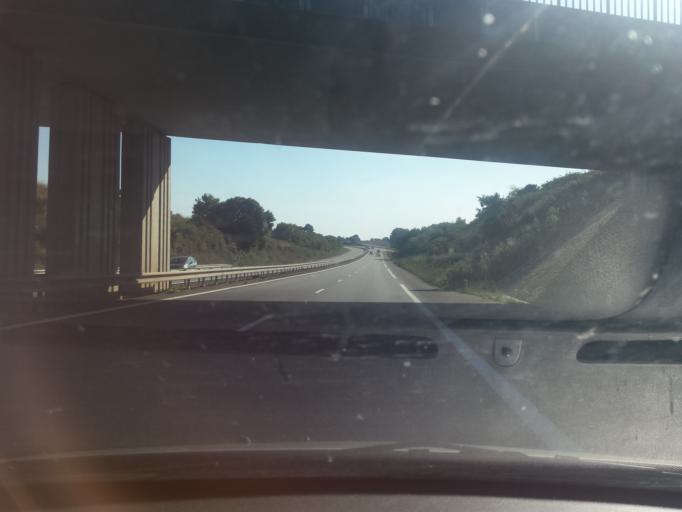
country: FR
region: Brittany
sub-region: Departement du Morbihan
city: Meucon
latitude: 47.7134
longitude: -2.7624
